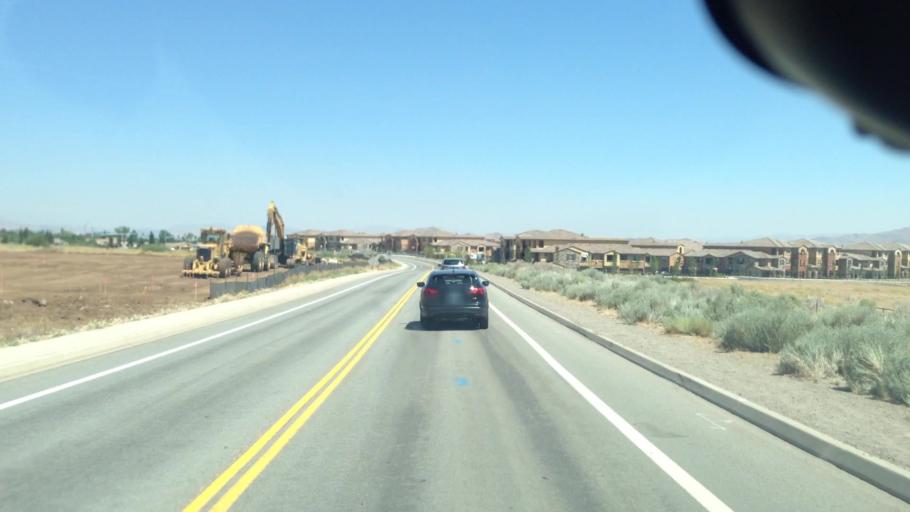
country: US
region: Nevada
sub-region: Washoe County
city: Sparks
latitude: 39.4048
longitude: -119.7597
